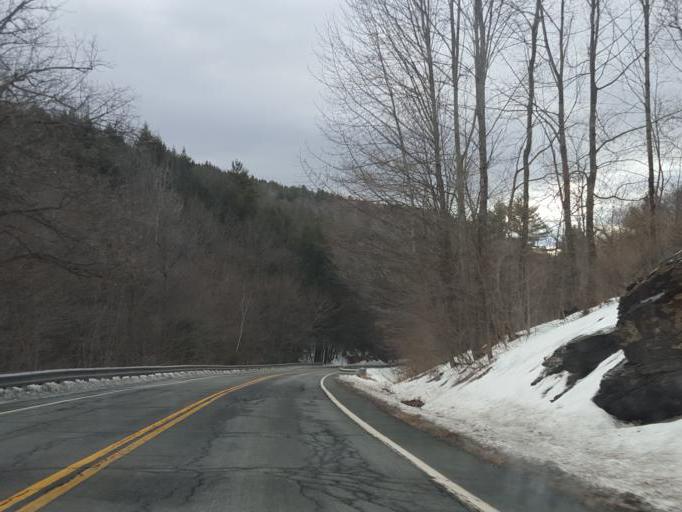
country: US
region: Vermont
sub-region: Windsor County
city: Woodstock
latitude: 43.5764
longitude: -72.4442
